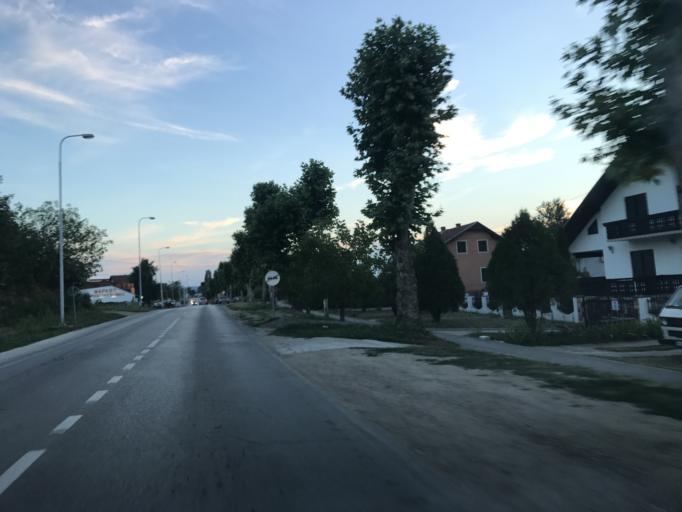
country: RS
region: Central Serbia
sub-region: Branicevski Okrug
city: Veliko Gradiste
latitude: 44.7565
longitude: 21.5039
